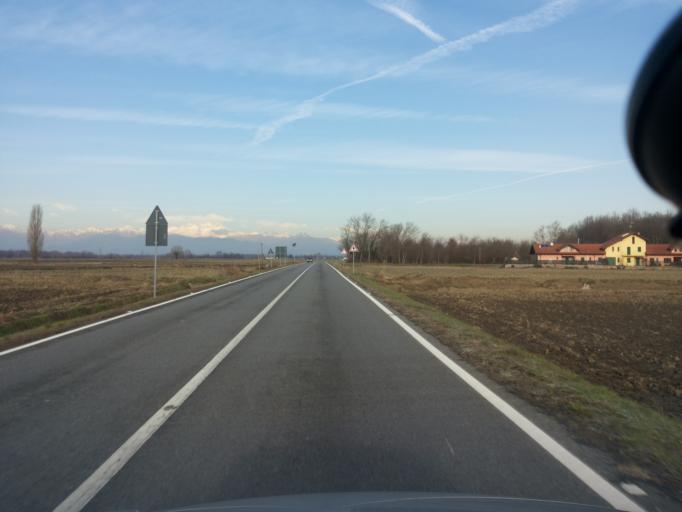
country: IT
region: Piedmont
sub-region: Provincia di Vercelli
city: Albano Vercellese
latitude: 45.4217
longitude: 8.3790
